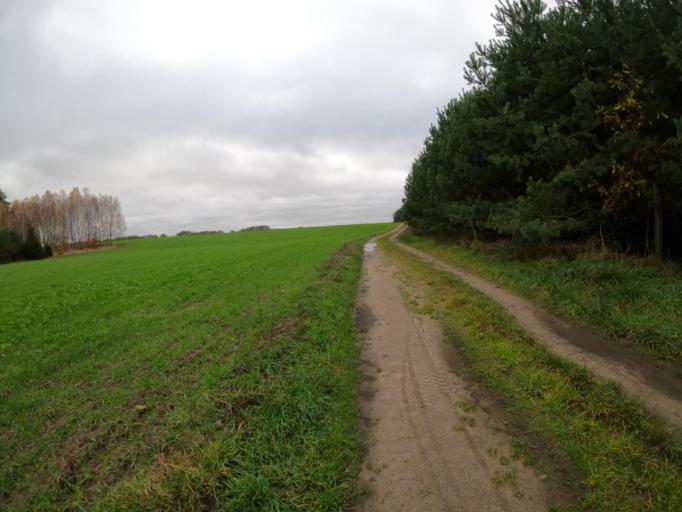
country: PL
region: West Pomeranian Voivodeship
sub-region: Powiat walecki
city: Tuczno
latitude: 53.2775
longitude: 16.1514
